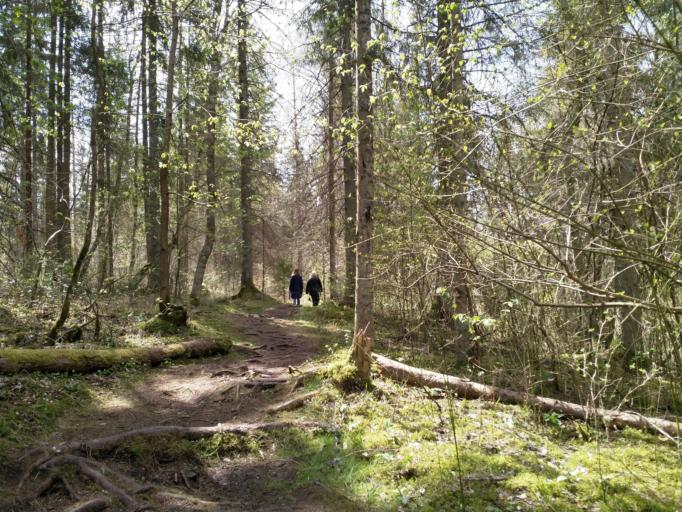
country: LV
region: Kandava
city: Kandava
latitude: 57.0235
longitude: 22.7766
